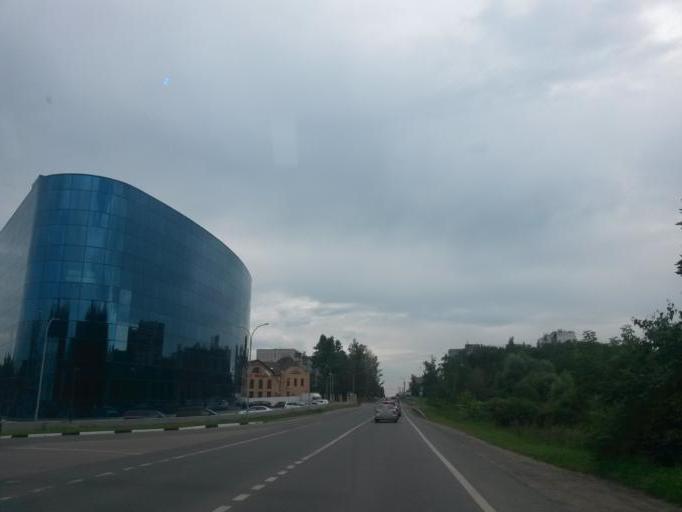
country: RU
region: Moskovskaya
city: Vostryakovo
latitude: 55.4193
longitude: 37.8403
